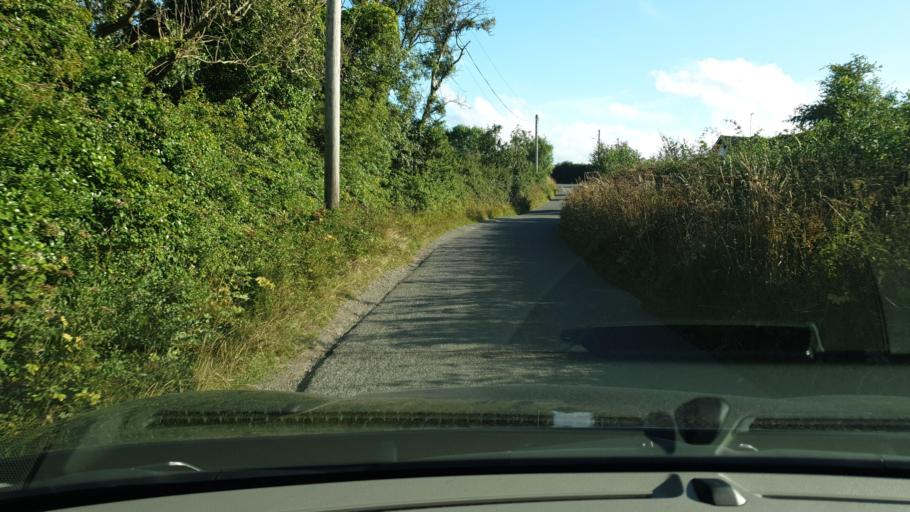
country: IE
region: Leinster
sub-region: An Mhi
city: Stamullin
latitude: 53.5830
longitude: -6.2456
